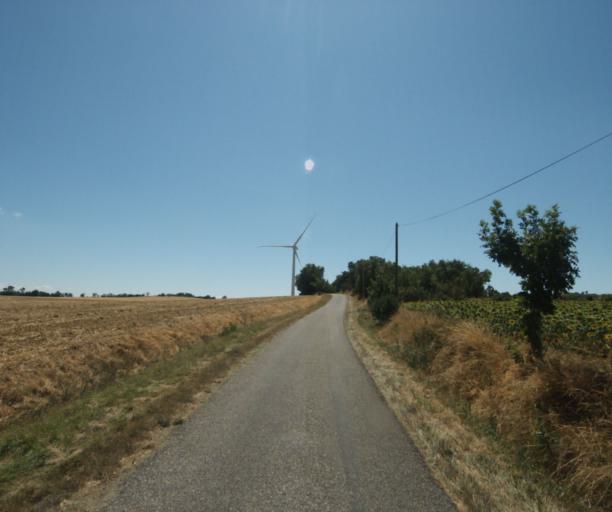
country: FR
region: Midi-Pyrenees
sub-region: Departement de la Haute-Garonne
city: Saint-Felix-Lauragais
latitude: 43.4597
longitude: 1.9044
